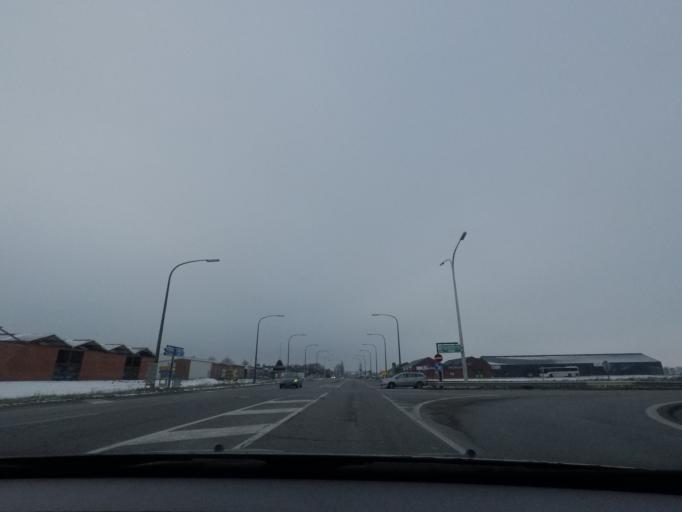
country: BE
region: Wallonia
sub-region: Province de Namur
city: Floreffe
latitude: 50.4938
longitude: 4.7231
